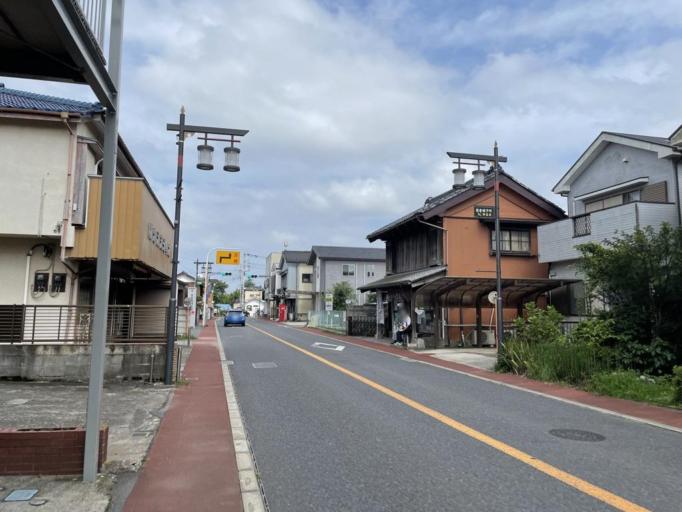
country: JP
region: Chiba
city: Sakura
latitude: 35.7197
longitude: 140.2323
